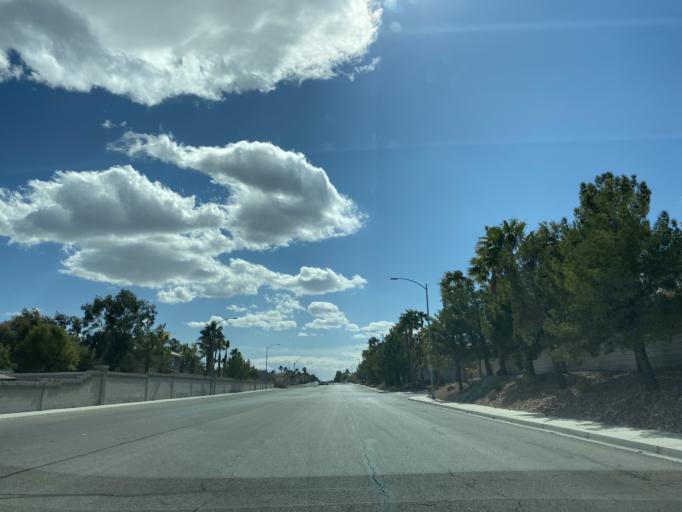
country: US
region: Nevada
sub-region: Clark County
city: Summerlin South
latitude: 36.2360
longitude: -115.2884
